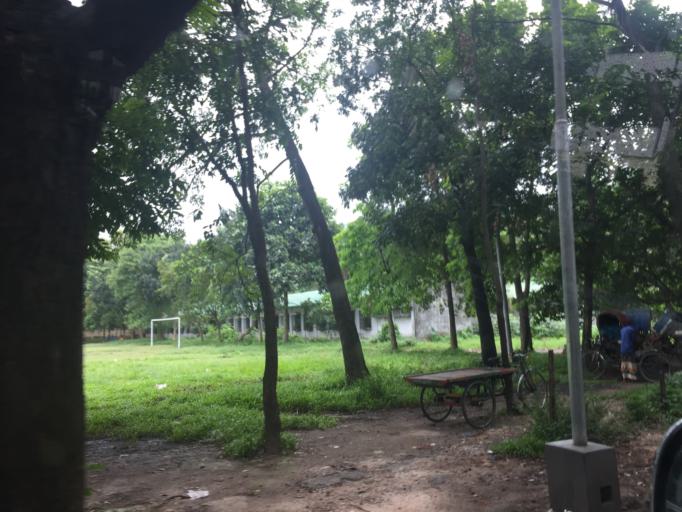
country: BD
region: Dhaka
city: Azimpur
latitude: 23.7338
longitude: 90.3895
